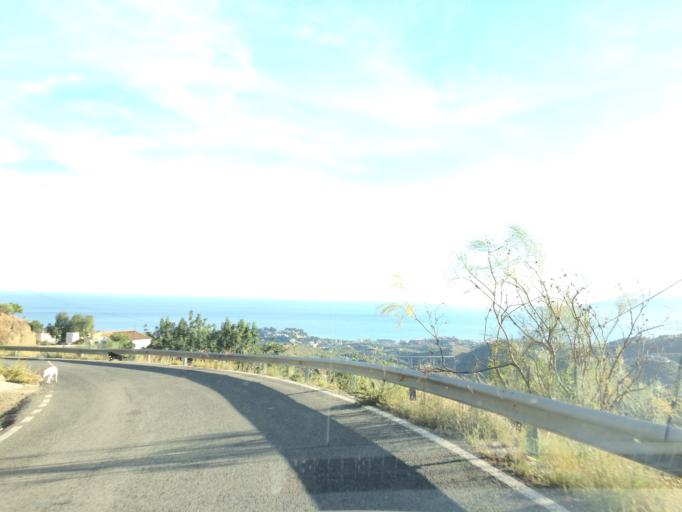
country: ES
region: Andalusia
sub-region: Provincia de Malaga
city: Totalan
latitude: 36.7476
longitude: -4.3305
